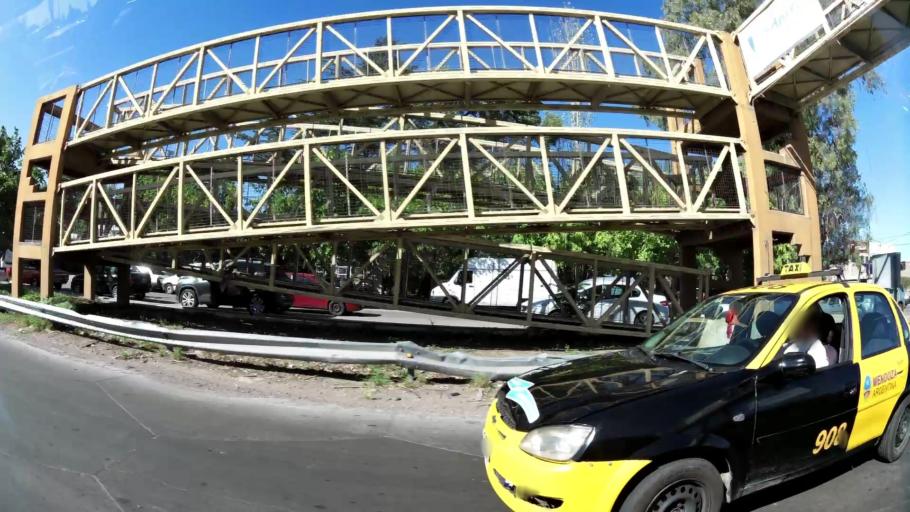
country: AR
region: Mendoza
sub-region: Departamento de Godoy Cruz
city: Godoy Cruz
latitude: -32.9256
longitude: -68.8267
